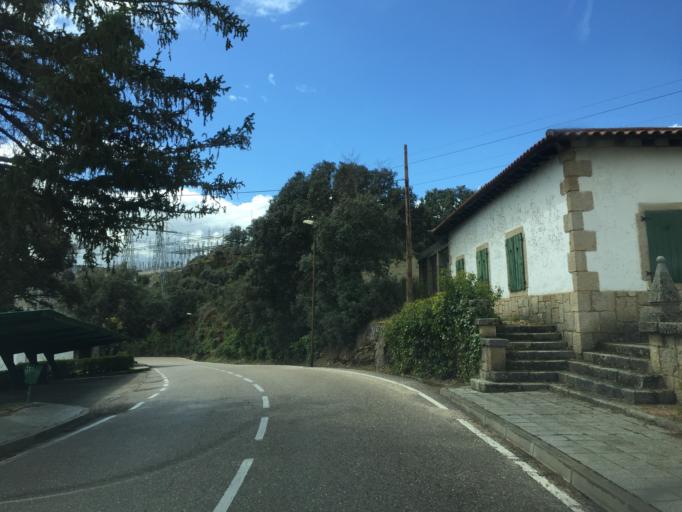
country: ES
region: Castille and Leon
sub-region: Provincia de Zamora
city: Moral de Sayago
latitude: 41.4936
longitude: -6.0881
